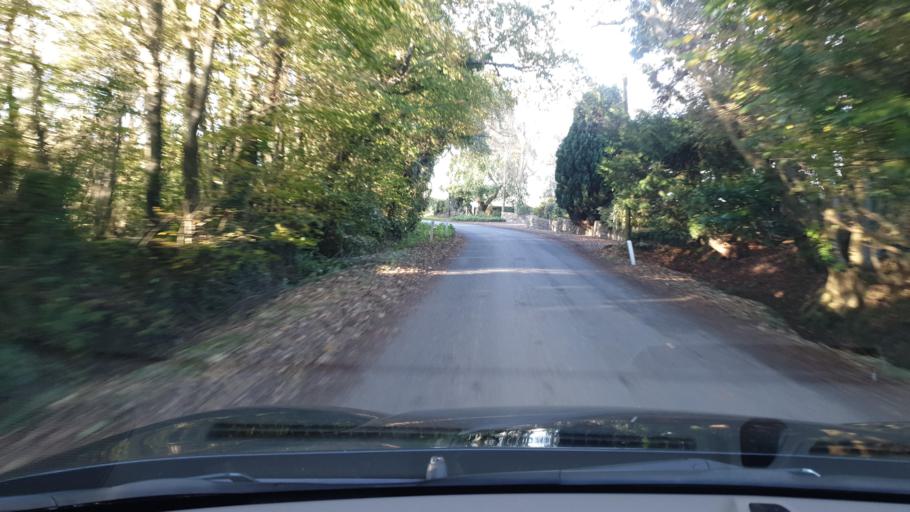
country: IE
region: Leinster
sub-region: An Mhi
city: Stamullin
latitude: 53.6224
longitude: -6.2625
